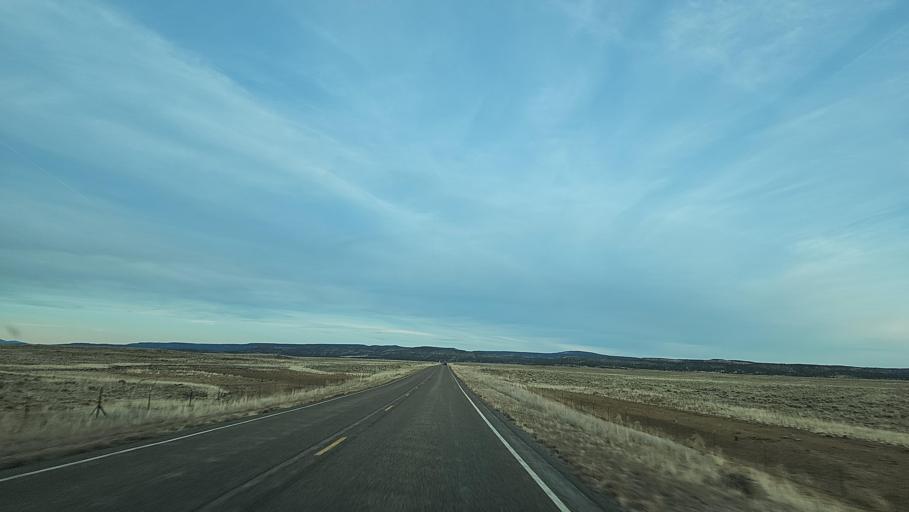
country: US
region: New Mexico
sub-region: Cibola County
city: Grants
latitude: 34.6998
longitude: -108.0380
